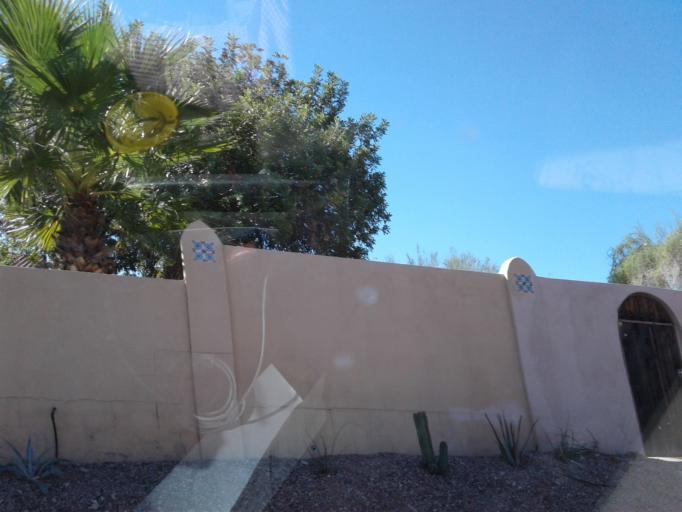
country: US
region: Arizona
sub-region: Maricopa County
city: Paradise Valley
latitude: 33.5880
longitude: -112.0327
